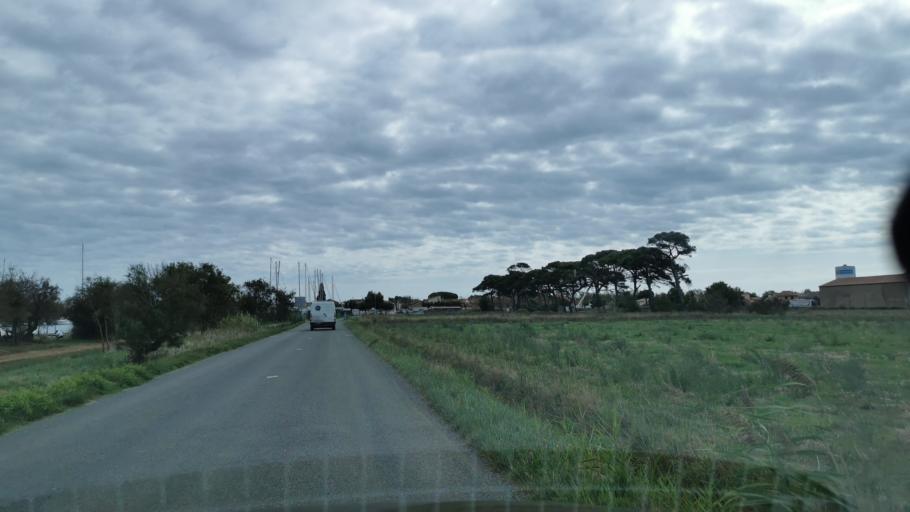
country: FR
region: Languedoc-Roussillon
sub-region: Departement de l'Herault
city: Vendres
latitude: 43.2191
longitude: 3.2262
